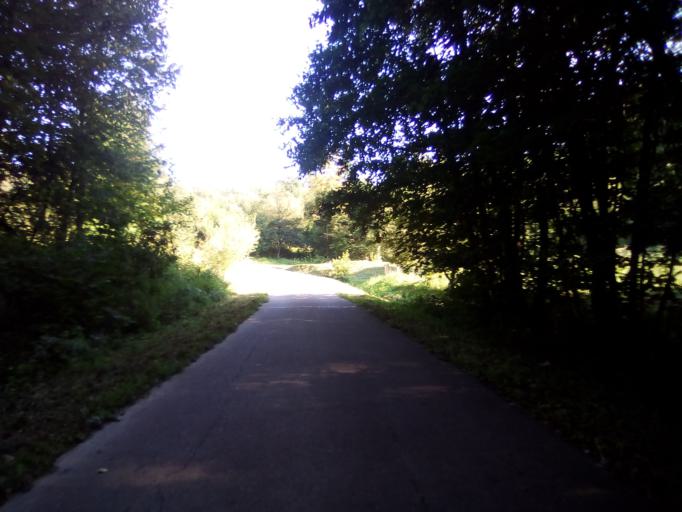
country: PL
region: Subcarpathian Voivodeship
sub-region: Powiat brzozowski
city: Domaradz
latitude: 49.8102
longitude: 21.9649
